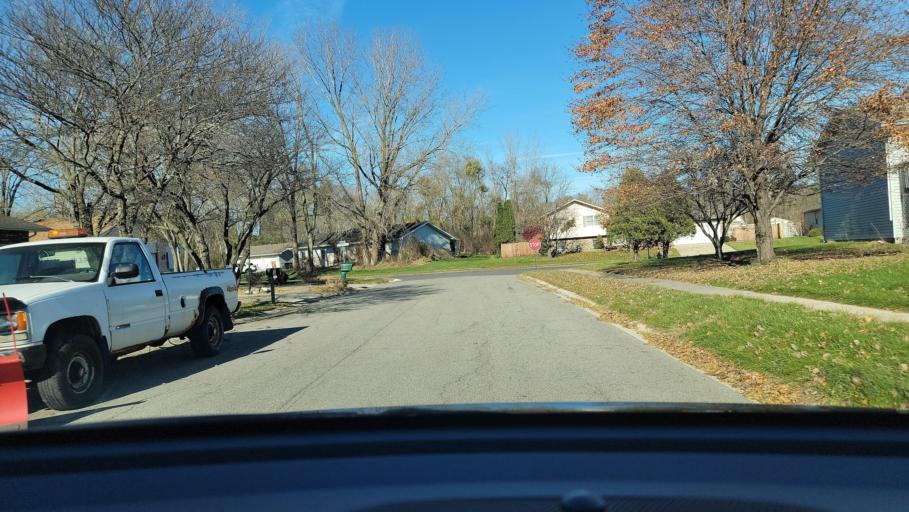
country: US
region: Indiana
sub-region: Porter County
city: Portage
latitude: 41.5888
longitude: -87.1965
